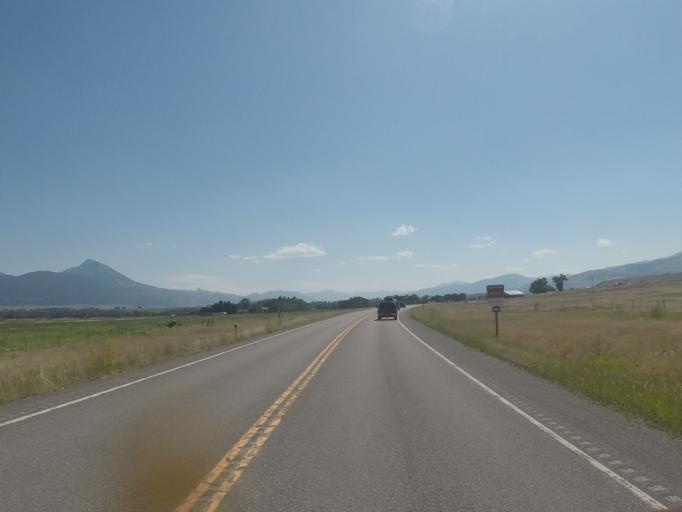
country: US
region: Montana
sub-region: Park County
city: Livingston
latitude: 45.4293
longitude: -110.6419
